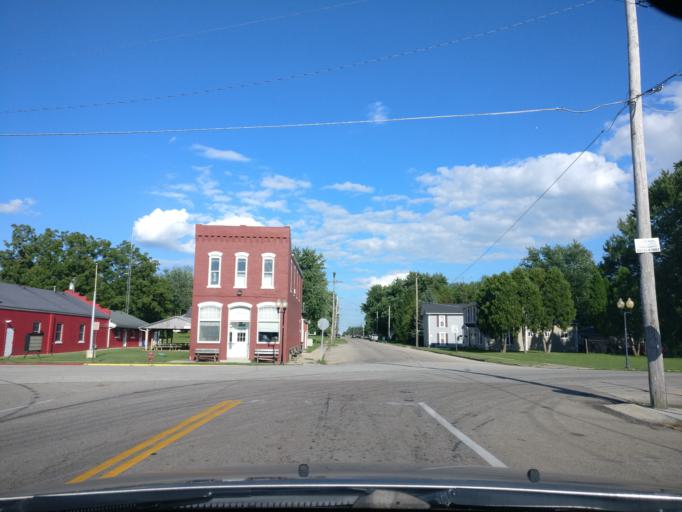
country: US
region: Ohio
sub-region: Greene County
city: Jamestown
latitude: 39.5804
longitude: -83.7247
